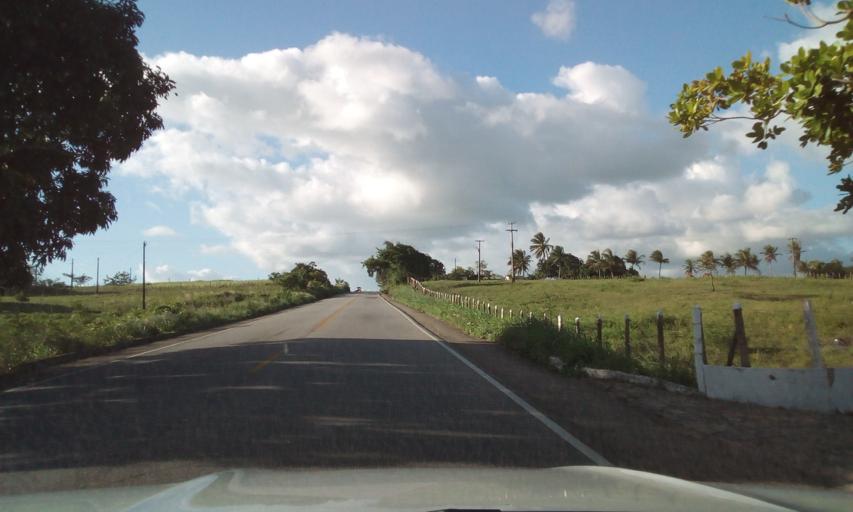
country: BR
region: Paraiba
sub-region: Pilar
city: Pilar
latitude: -7.1813
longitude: -35.2303
